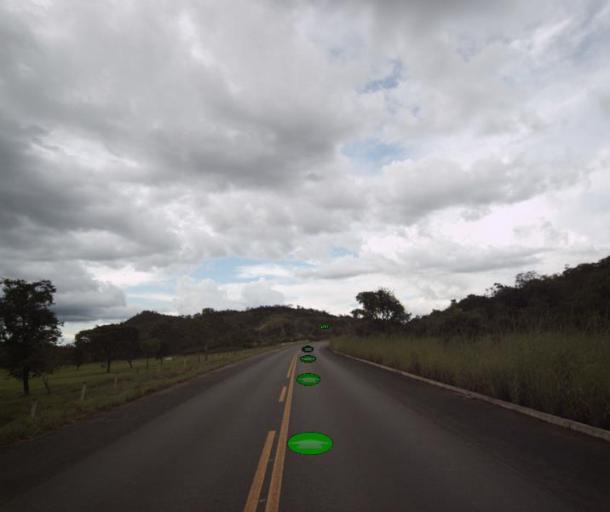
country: BR
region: Goias
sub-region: Niquelandia
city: Niquelandia
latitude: -14.5060
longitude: -48.5194
